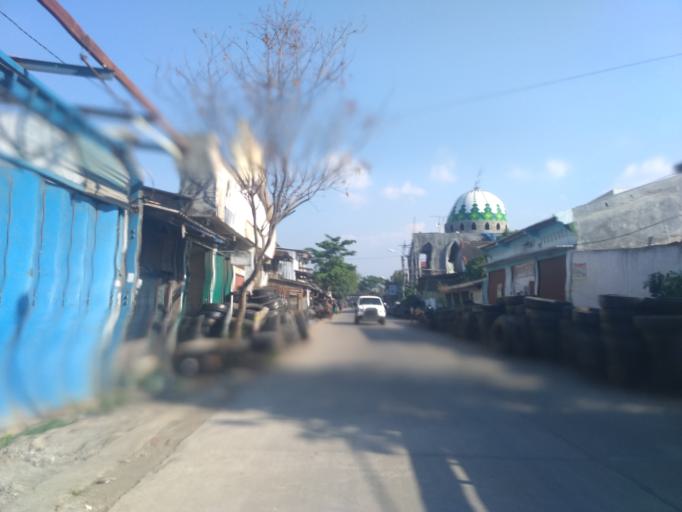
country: ID
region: Central Java
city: Semarang
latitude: -6.9701
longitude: 110.4427
